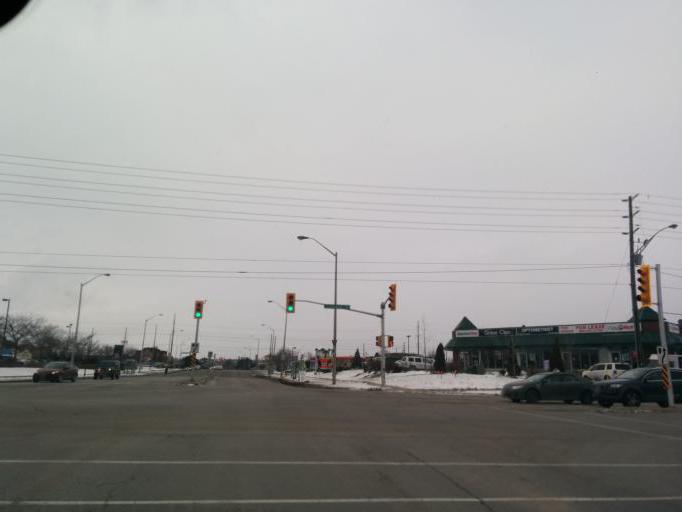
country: CA
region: Ontario
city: Oakville
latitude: 43.4881
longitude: -79.6502
